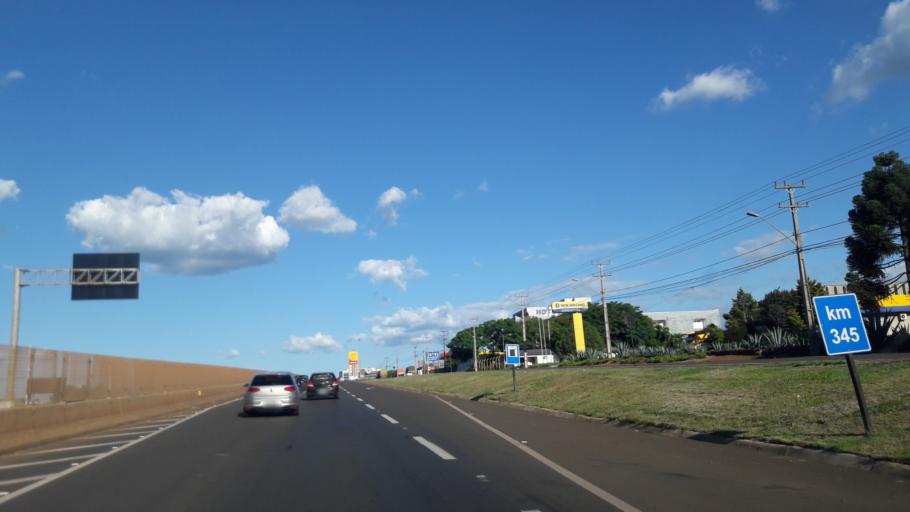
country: BR
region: Parana
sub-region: Guarapuava
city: Guarapuava
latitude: -25.3659
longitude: -51.4856
